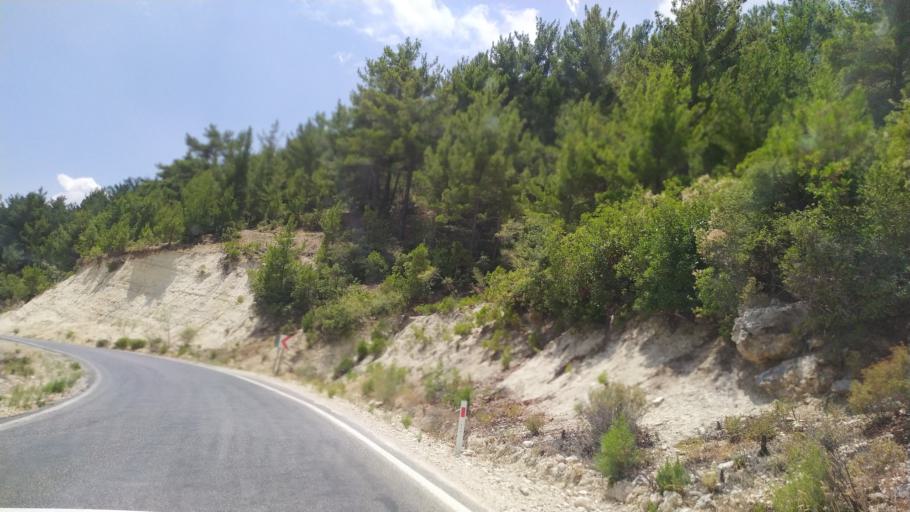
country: TR
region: Mersin
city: Gulnar
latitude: 36.2975
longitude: 33.3795
